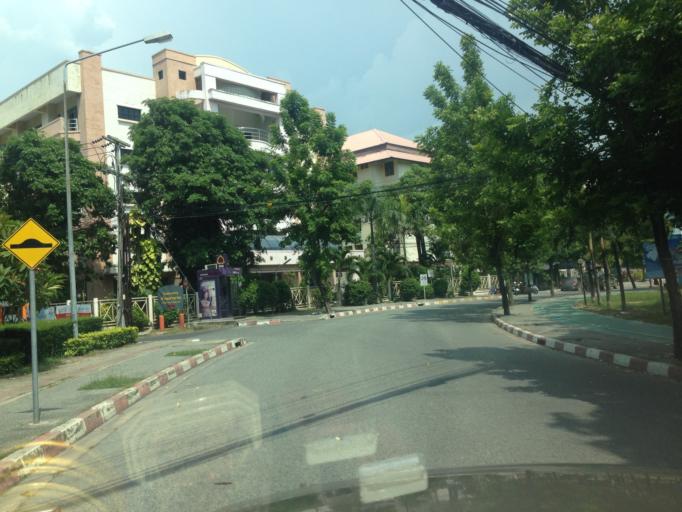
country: TH
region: Chon Buri
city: Chon Buri
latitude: 13.2777
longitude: 100.9276
